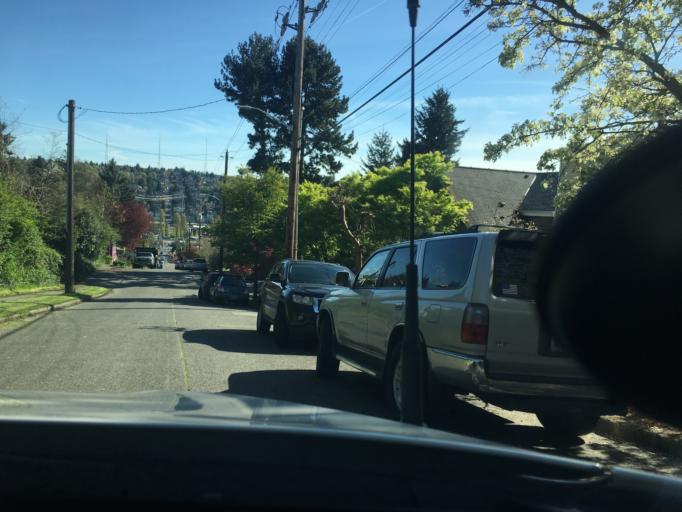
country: US
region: Washington
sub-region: King County
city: Seattle
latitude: 47.6571
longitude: -122.3545
